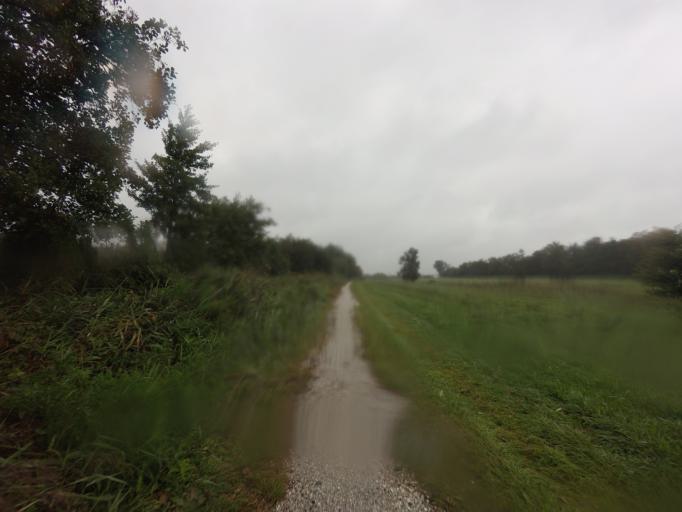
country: NL
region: Friesland
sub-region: Gemeente Smallingerland
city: Oudega
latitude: 53.0992
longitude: 5.9819
